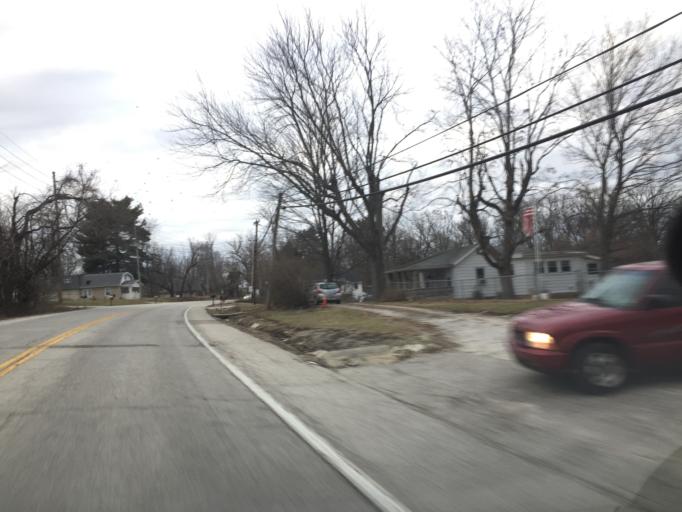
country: US
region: Indiana
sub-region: Monroe County
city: Bloomington
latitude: 39.1818
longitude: -86.5497
